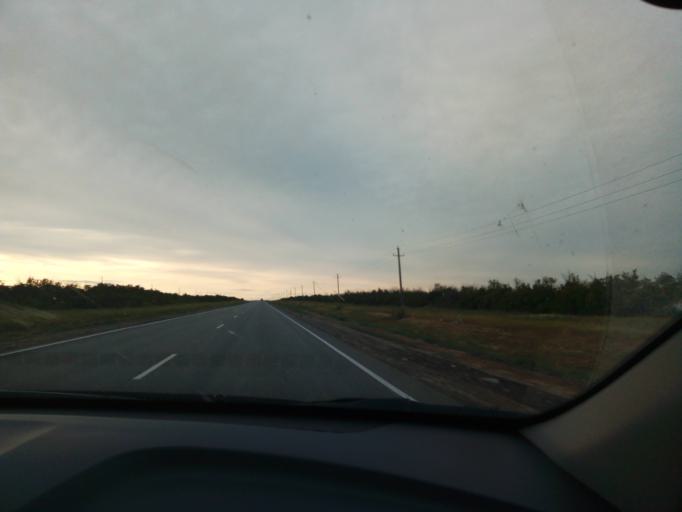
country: RU
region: Volgograd
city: Primorsk
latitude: 49.2757
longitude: 44.8740
